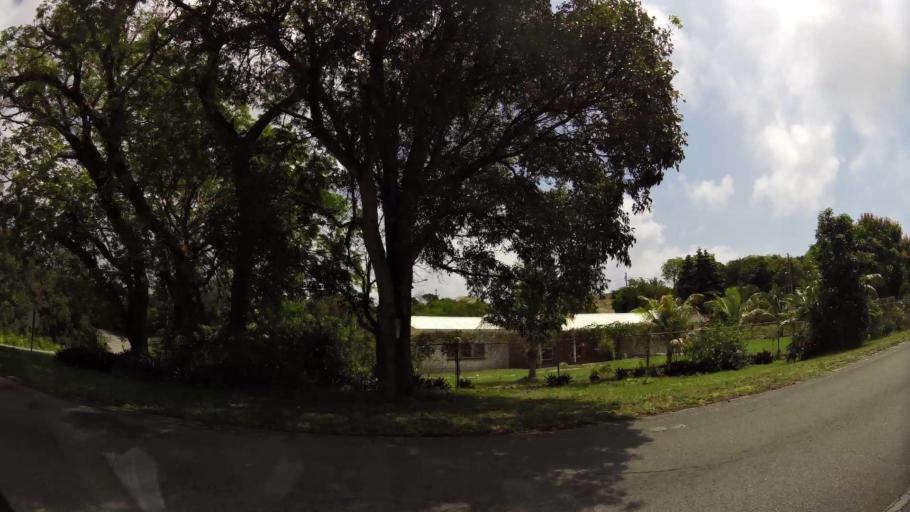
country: BS
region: Freeport
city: Lucaya
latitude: 26.5191
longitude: -78.6498
